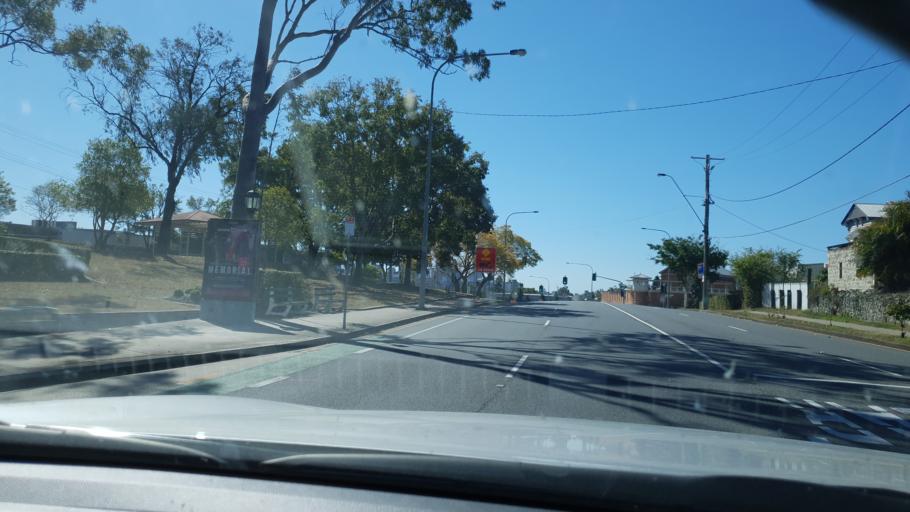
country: AU
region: Queensland
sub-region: Brisbane
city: Woolloongabba
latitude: -27.4971
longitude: 153.0276
